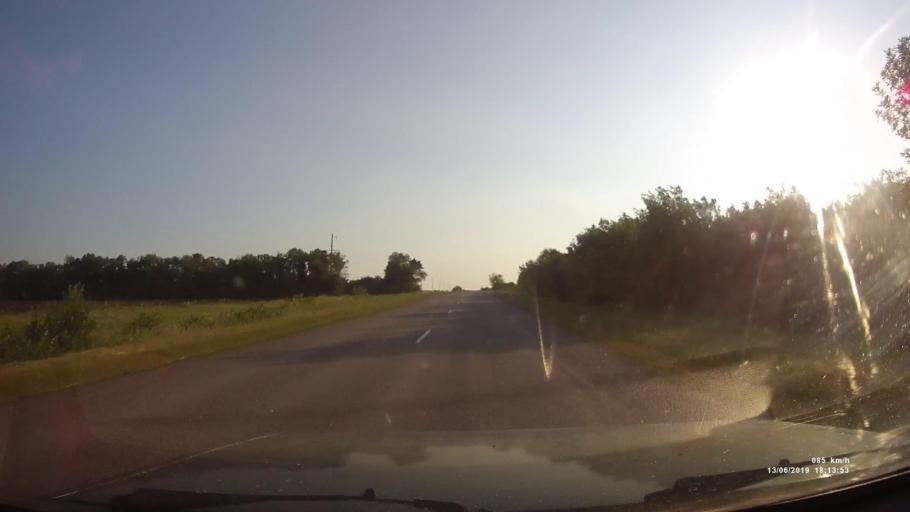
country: RU
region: Rostov
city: Kazanskaya
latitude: 49.9365
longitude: 41.3865
